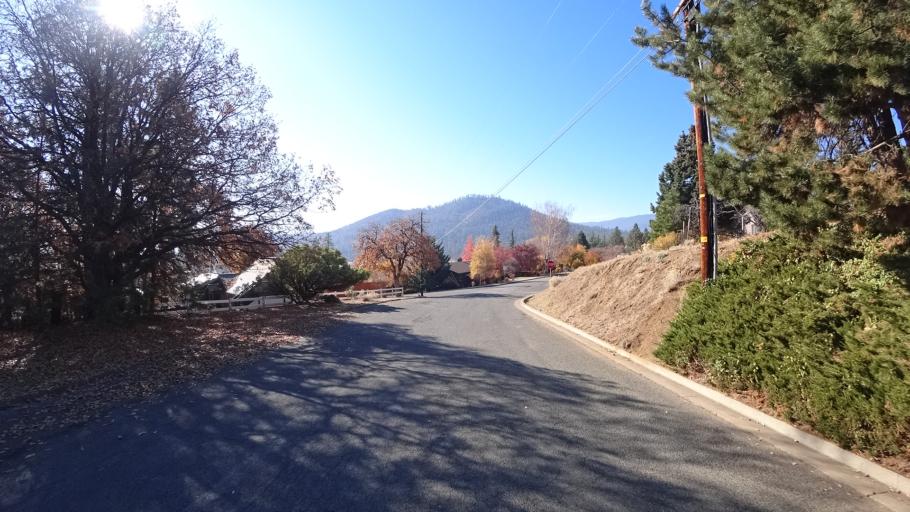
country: US
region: California
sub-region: Siskiyou County
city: Yreka
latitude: 41.7394
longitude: -122.6575
